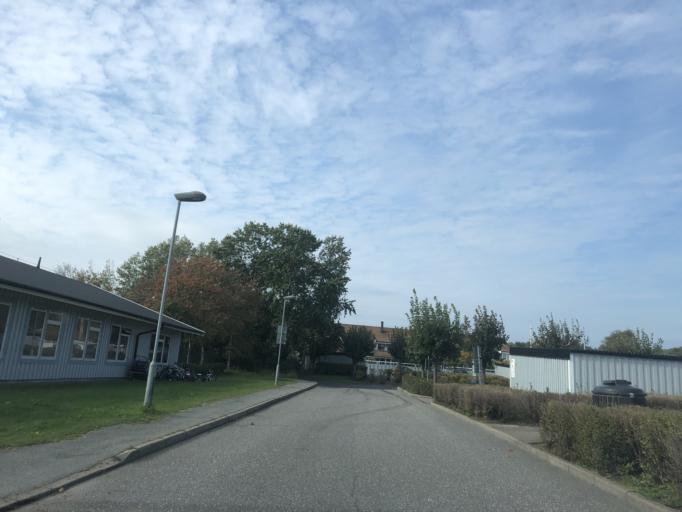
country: SE
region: Vaestra Goetaland
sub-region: Goteborg
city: Majorna
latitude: 57.6488
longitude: 11.8771
